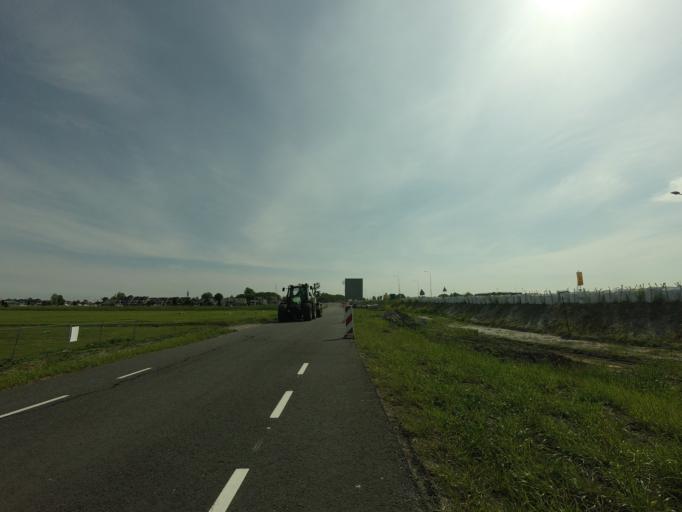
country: NL
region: North Holland
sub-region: Gemeente Zaanstad
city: Zaanstad
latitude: 52.5214
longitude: 4.7856
